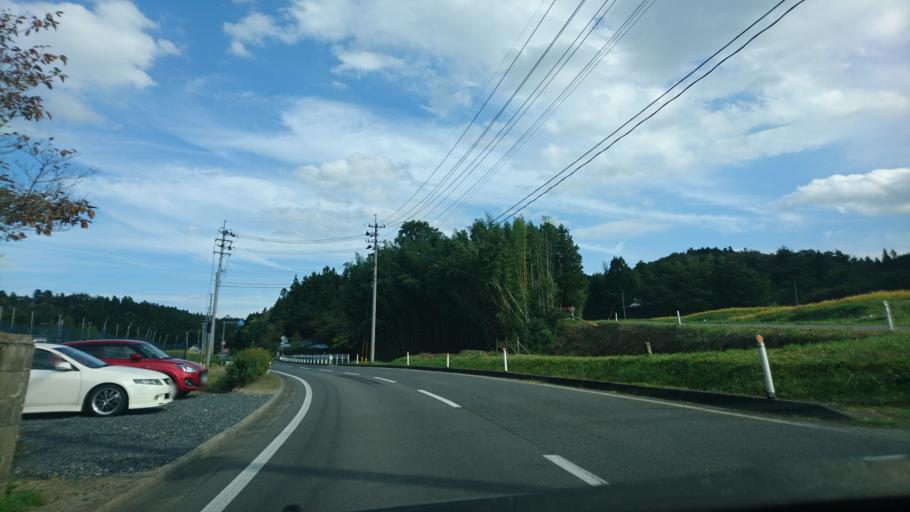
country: JP
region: Iwate
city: Ichinoseki
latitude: 38.8336
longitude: 141.2104
